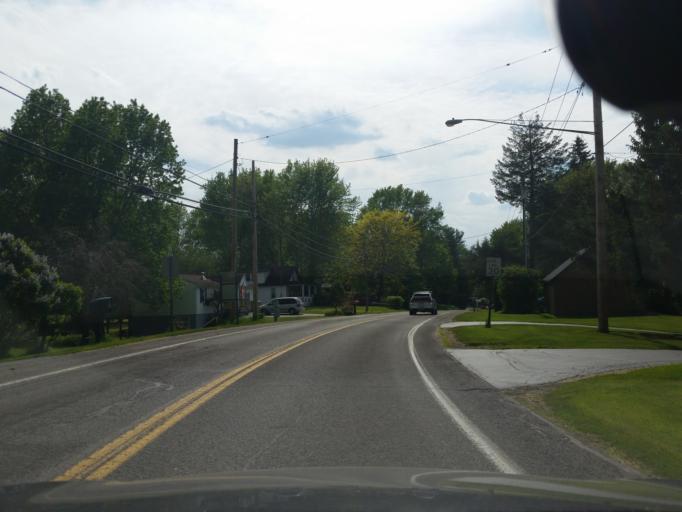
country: US
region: New York
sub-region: Chautauqua County
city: Lakewood
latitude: 42.0999
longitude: -79.3442
